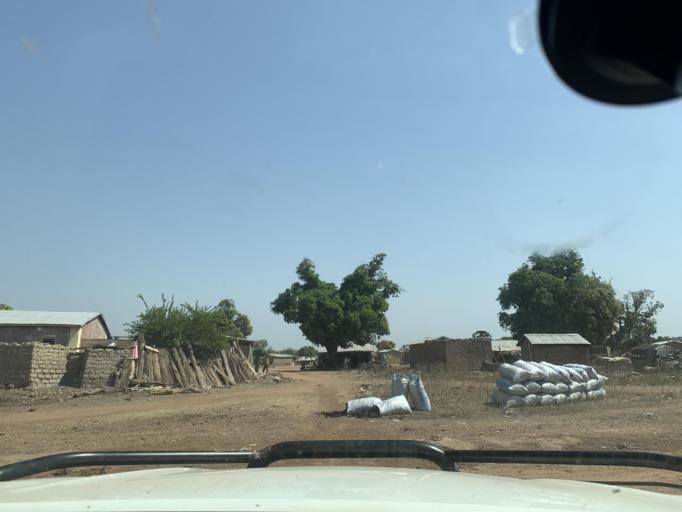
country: ML
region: Sikasso
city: Kolondieba
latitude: 10.8292
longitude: -6.7237
